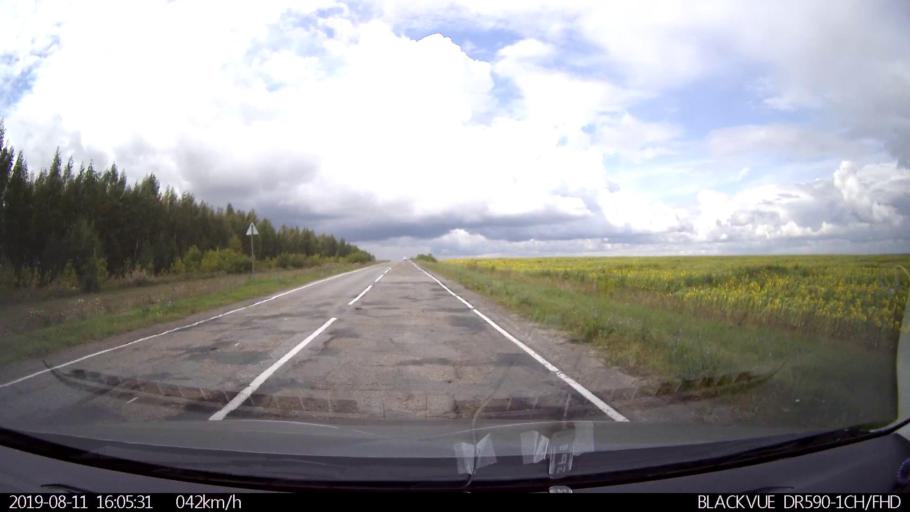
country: RU
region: Ulyanovsk
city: Ignatovka
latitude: 53.9613
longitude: 47.6490
